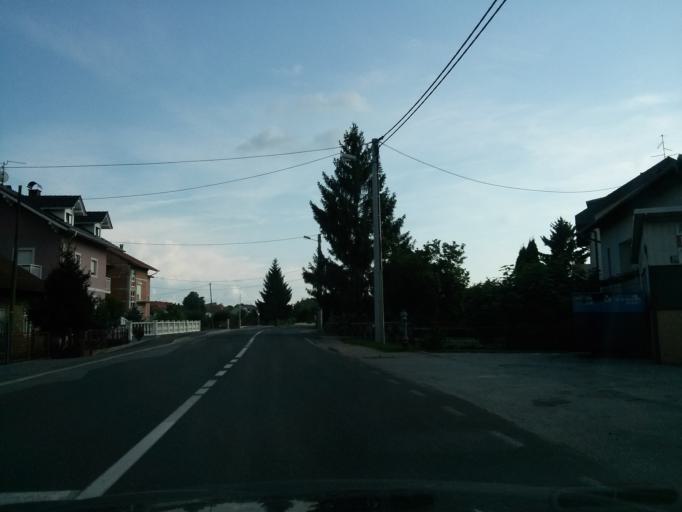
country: HR
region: Grad Zagreb
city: Zadvorsko
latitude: 45.7574
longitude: 15.9325
